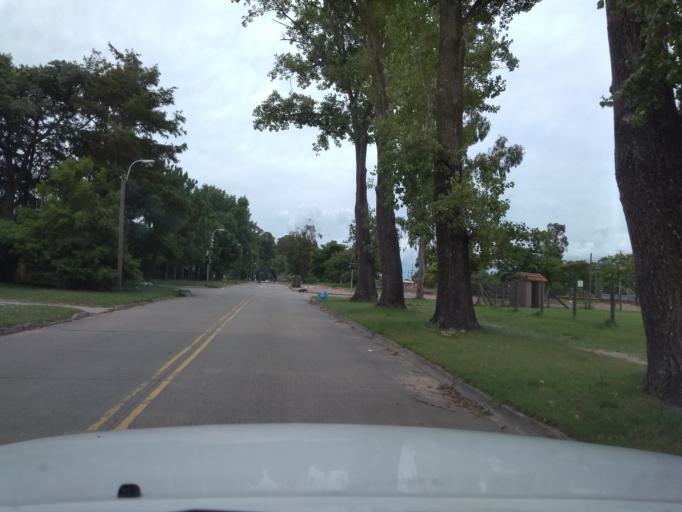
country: UY
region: Canelones
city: Paso de Carrasco
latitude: -34.8700
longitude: -56.0591
